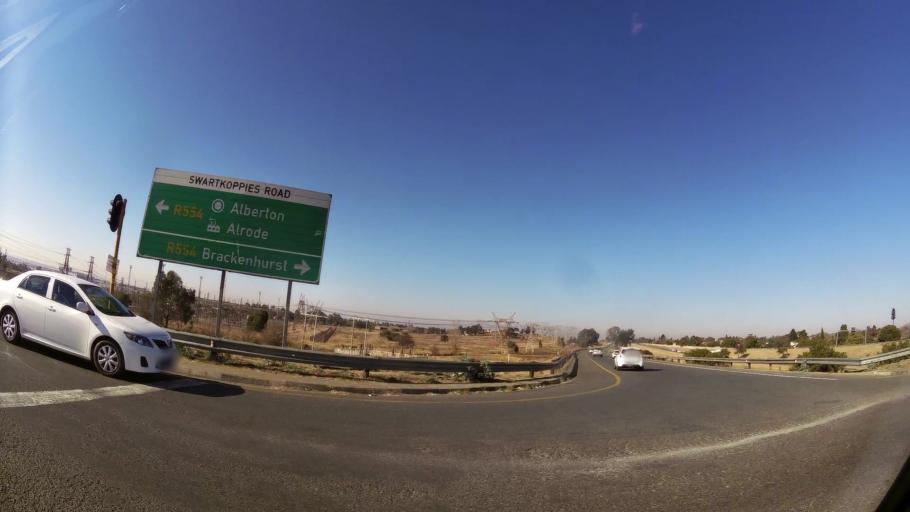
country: ZA
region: Gauteng
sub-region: Ekurhuleni Metropolitan Municipality
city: Germiston
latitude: -26.3057
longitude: 28.1125
